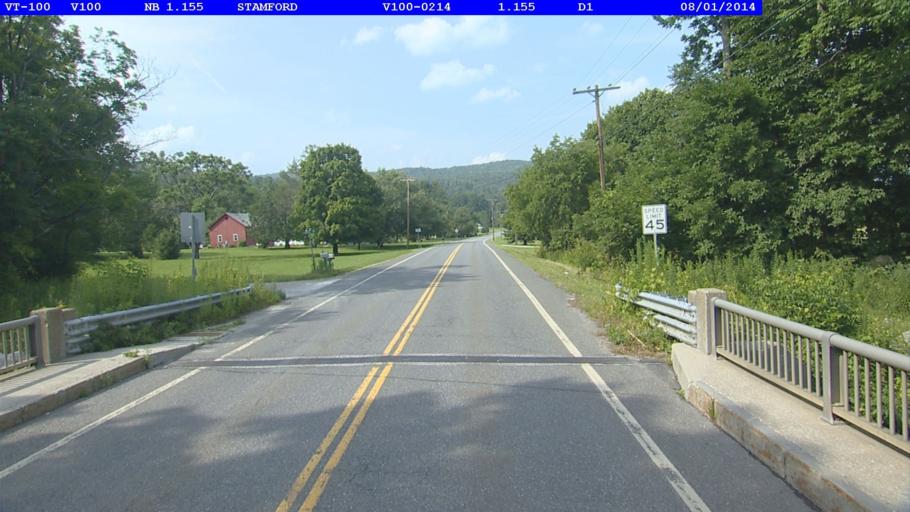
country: US
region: Massachusetts
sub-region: Berkshire County
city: North Adams
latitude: 42.7573
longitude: -73.0677
